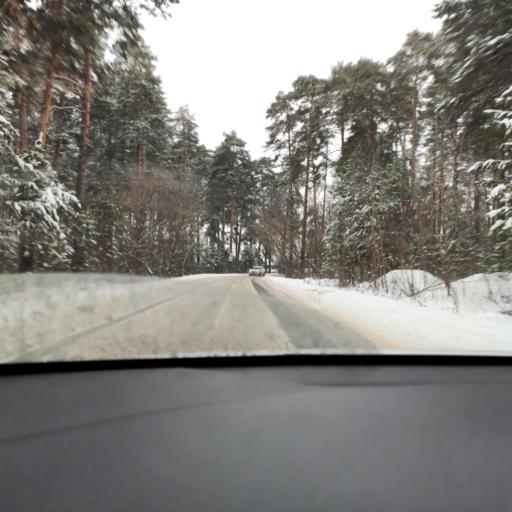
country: RU
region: Tatarstan
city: Osinovo
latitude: 55.8235
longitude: 48.8727
